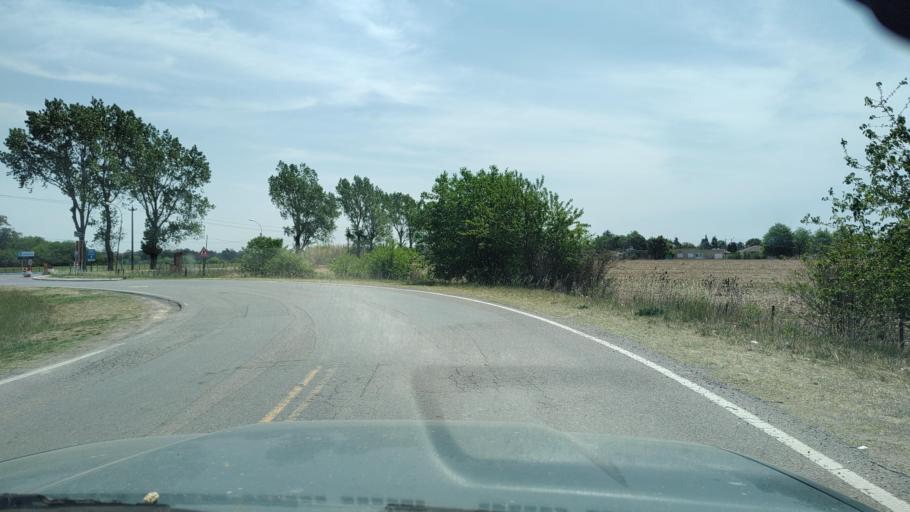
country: AR
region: Buenos Aires
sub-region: Partido de Lujan
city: Lujan
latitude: -34.6059
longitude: -59.1725
